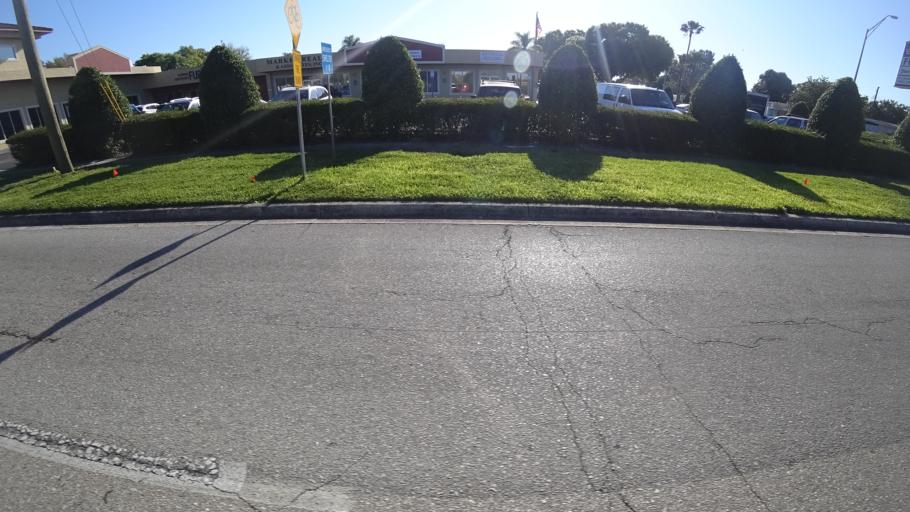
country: US
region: Florida
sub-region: Manatee County
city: Bayshore Gardens
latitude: 27.4315
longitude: -82.5877
